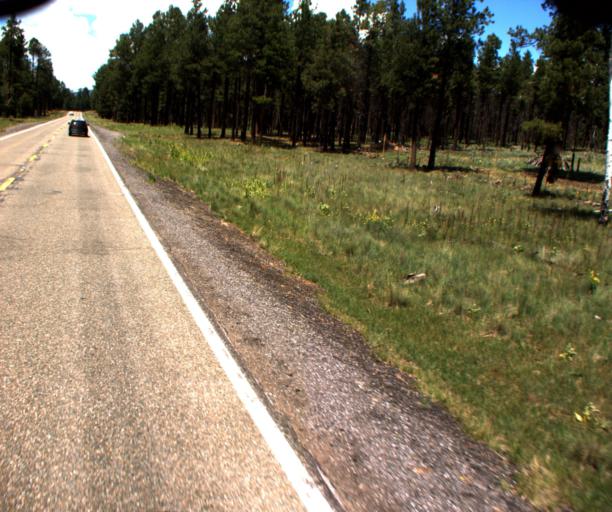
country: US
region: Arizona
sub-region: Coconino County
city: Flagstaff
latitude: 35.3282
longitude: -111.7762
